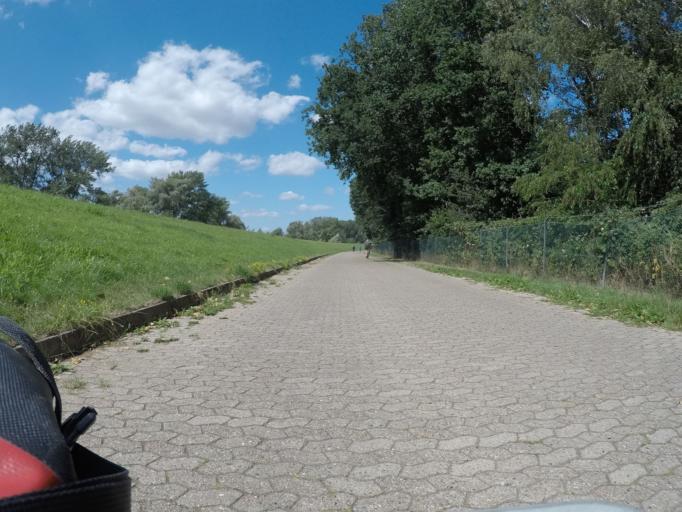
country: DE
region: Hamburg
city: Rothenburgsort
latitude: 53.5018
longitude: 10.0678
